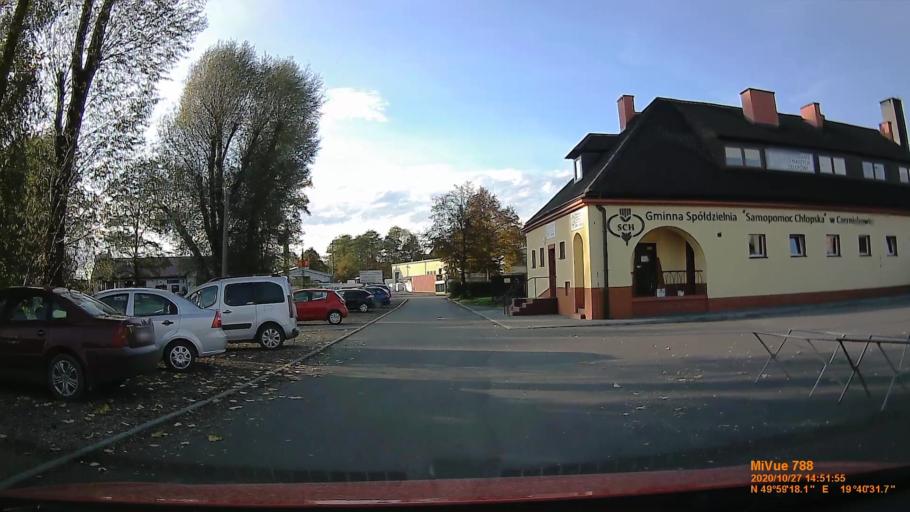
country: PL
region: Lesser Poland Voivodeship
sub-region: Powiat krakowski
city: Czernichow
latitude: 49.9884
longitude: 19.6755
